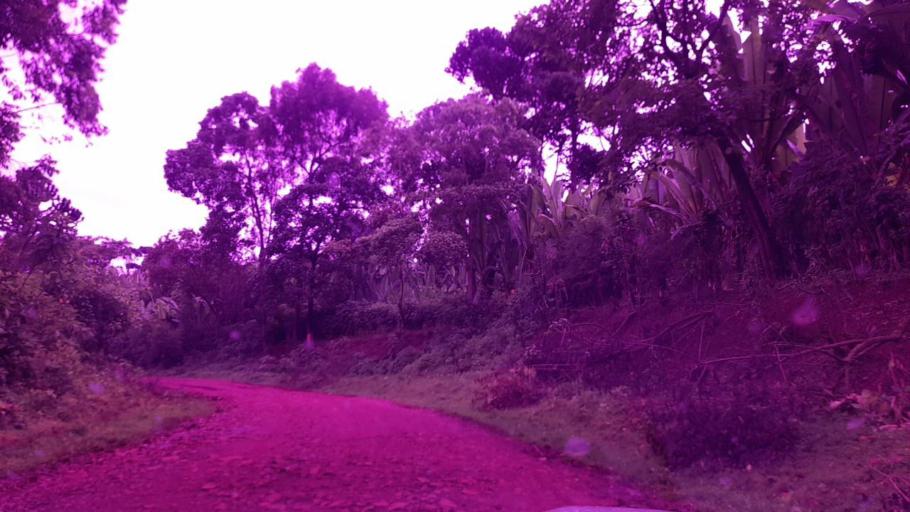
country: ET
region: Southern Nations, Nationalities, and People's Region
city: Tippi
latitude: 7.5797
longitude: 35.7766
